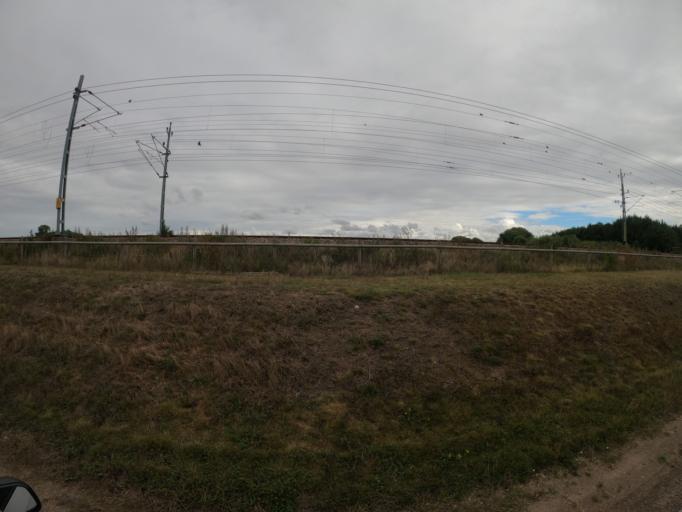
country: SE
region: Skane
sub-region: Lunds Kommun
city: Lund
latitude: 55.7388
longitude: 13.1558
